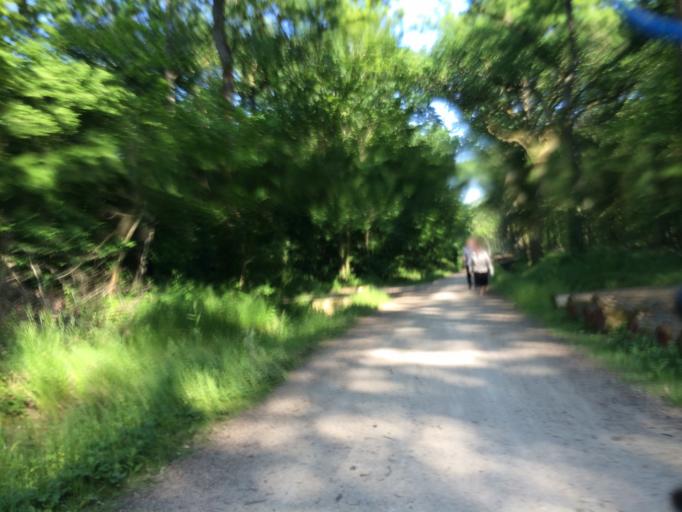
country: FR
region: Ile-de-France
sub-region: Departement de l'Essonne
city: Fleury-Merogis
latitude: 48.6295
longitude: 2.3685
